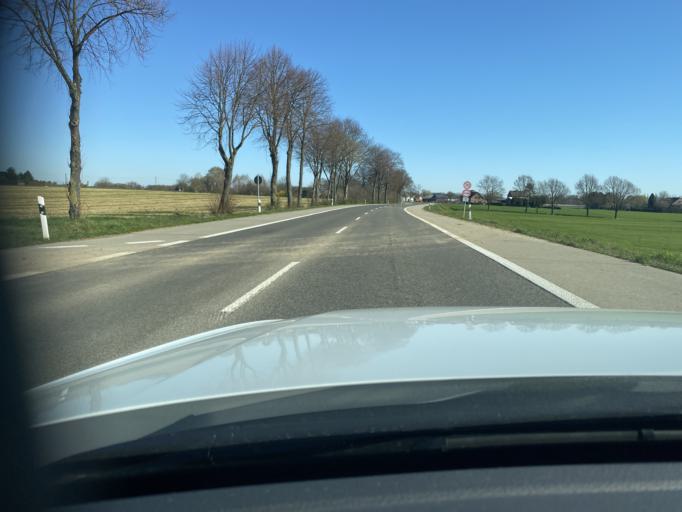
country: DE
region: North Rhine-Westphalia
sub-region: Regierungsbezirk Dusseldorf
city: Neubrueck
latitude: 51.1378
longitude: 6.6418
